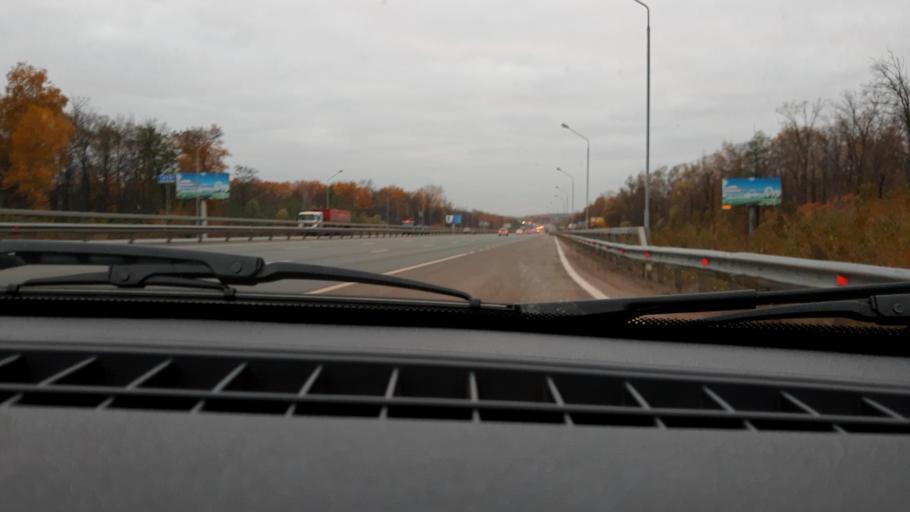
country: RU
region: Bashkortostan
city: Avdon
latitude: 54.6705
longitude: 55.8384
